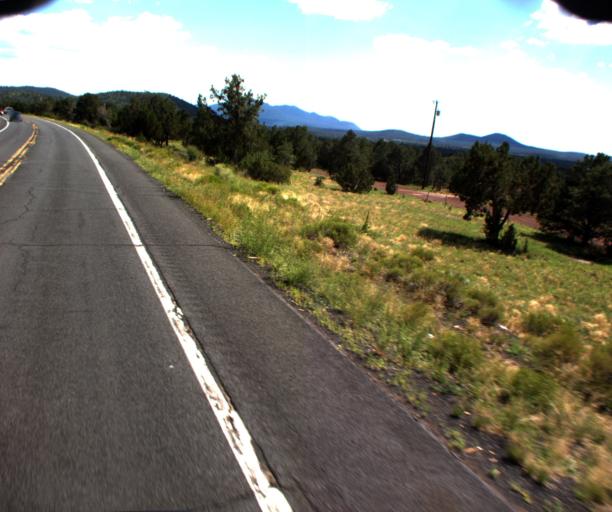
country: US
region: Arizona
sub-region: Coconino County
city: Williams
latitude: 35.3467
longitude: -112.1667
